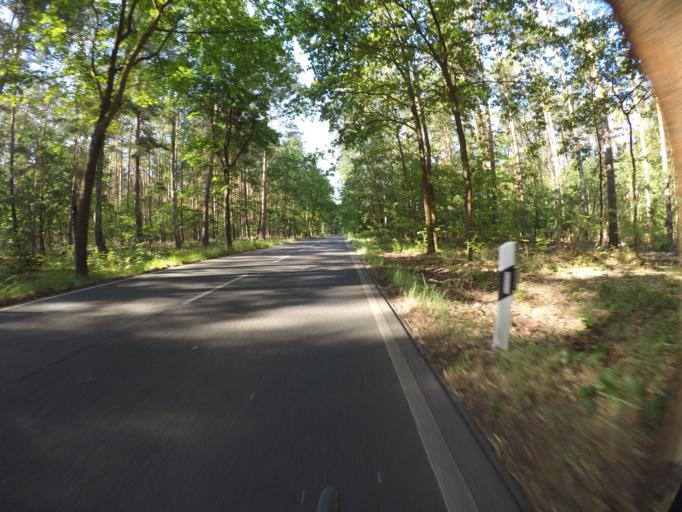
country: DE
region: Berlin
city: Schmockwitz
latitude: 52.3664
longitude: 13.6552
